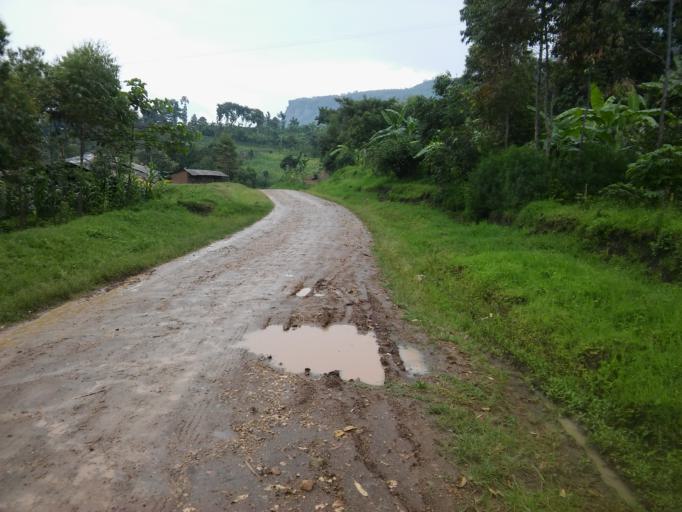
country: UG
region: Eastern Region
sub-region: Mbale District
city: Mbale
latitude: 1.0139
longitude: 34.2276
